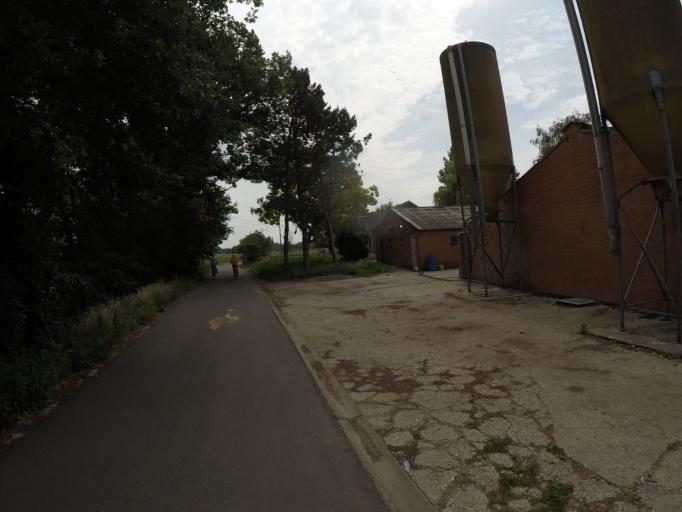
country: BE
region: Flanders
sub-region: Provincie Antwerpen
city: Essen
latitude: 51.4442
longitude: 4.5161
